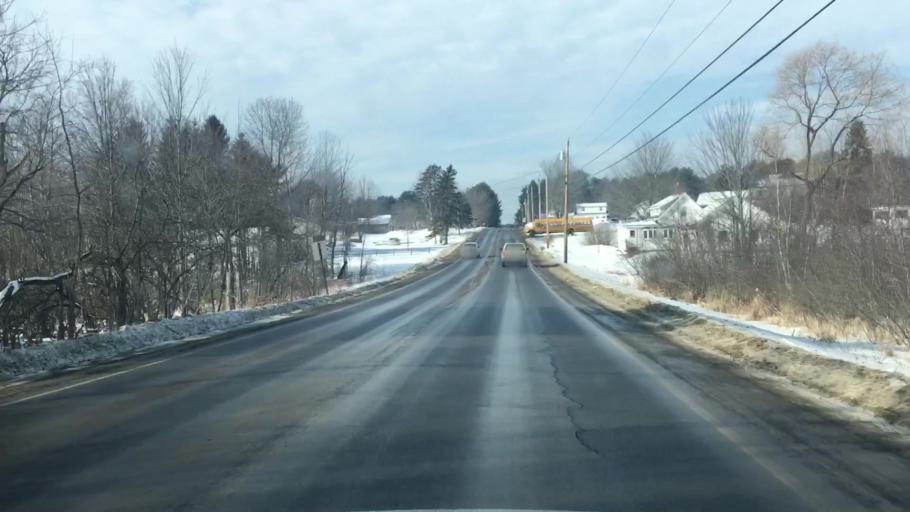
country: US
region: Maine
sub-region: Penobscot County
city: Hermon
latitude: 44.8502
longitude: -68.8791
